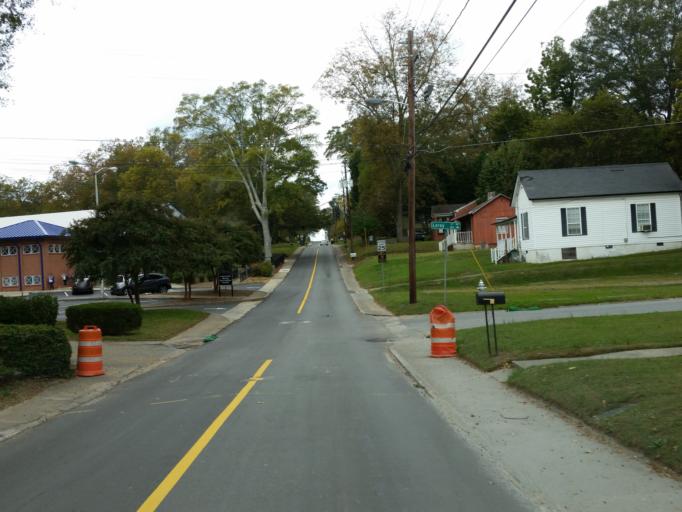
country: US
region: Georgia
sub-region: Cobb County
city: Marietta
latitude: 33.9531
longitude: -84.5363
